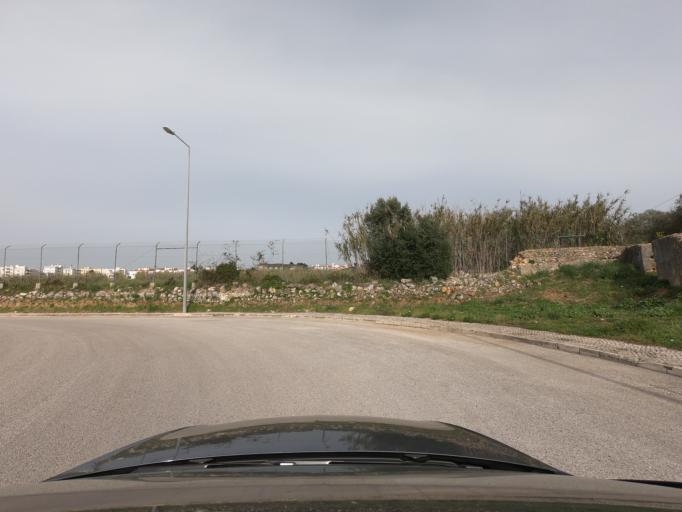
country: PT
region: Lisbon
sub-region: Cascais
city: Sao Domingos de Rana
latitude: 38.7021
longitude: -9.3217
